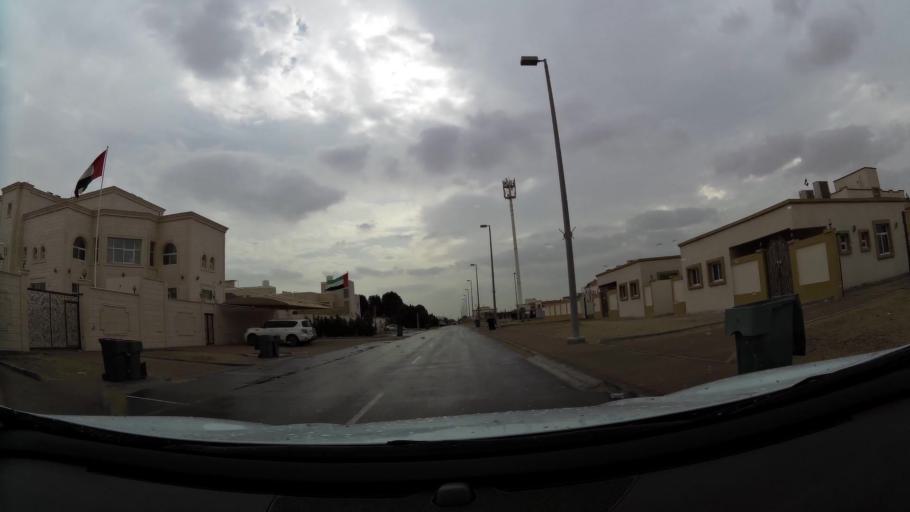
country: AE
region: Abu Dhabi
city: Abu Dhabi
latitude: 24.3654
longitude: 54.6256
